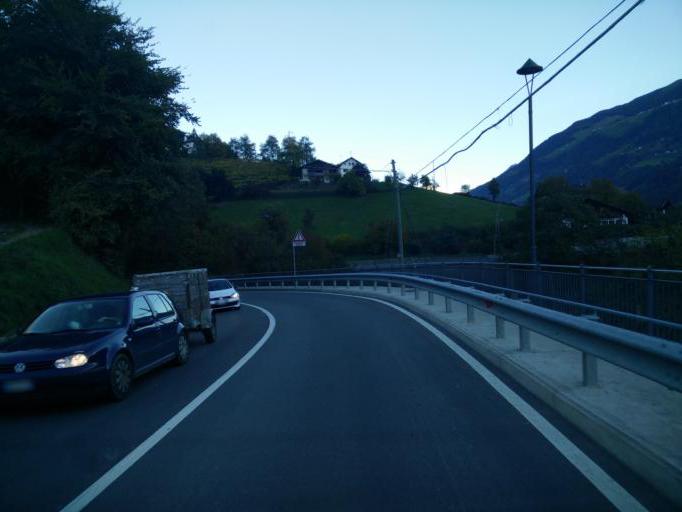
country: IT
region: Trentino-Alto Adige
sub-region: Bolzano
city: Rifiano
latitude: 46.7071
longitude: 11.1855
